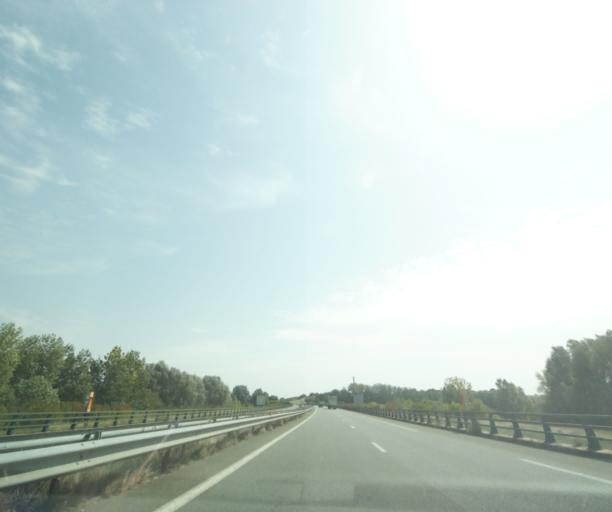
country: FR
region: Pays de la Loire
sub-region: Departement de la Vendee
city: Fontenay-le-Comte
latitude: 46.4409
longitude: -0.8433
